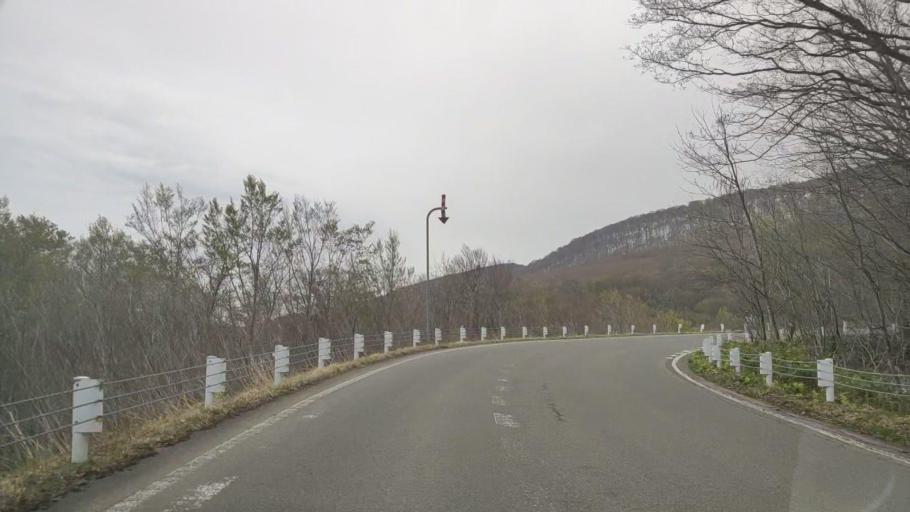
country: JP
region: Aomori
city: Aomori Shi
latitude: 40.6584
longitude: 140.9625
